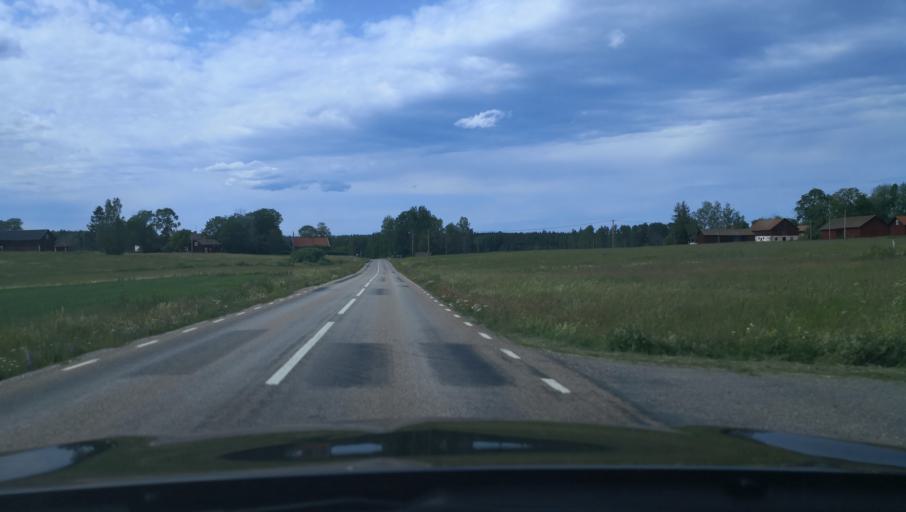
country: SE
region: Dalarna
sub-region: Avesta Kommun
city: Avesta
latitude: 59.9838
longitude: 16.1229
